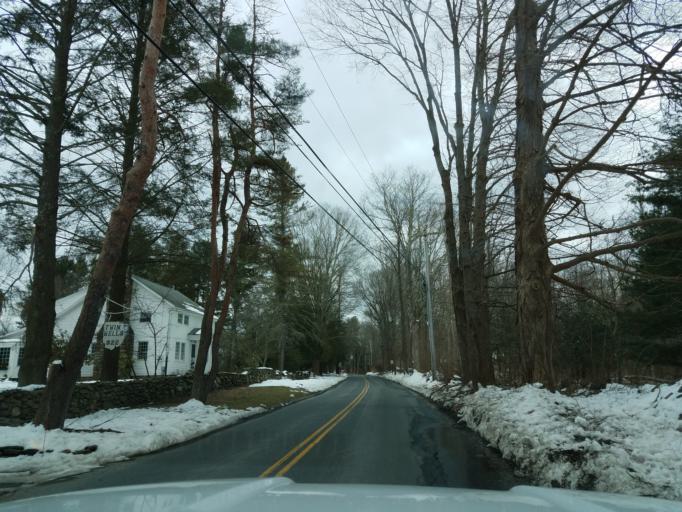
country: US
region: Connecticut
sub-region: Litchfield County
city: New Milford
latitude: 41.6188
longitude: -73.4306
